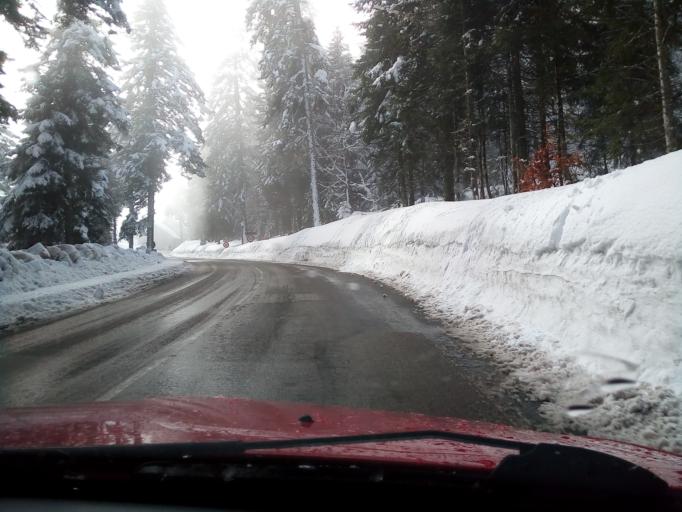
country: FR
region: Rhone-Alpes
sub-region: Departement de l'Isere
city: Le Sappey-en-Chartreuse
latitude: 45.2944
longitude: 5.7679
